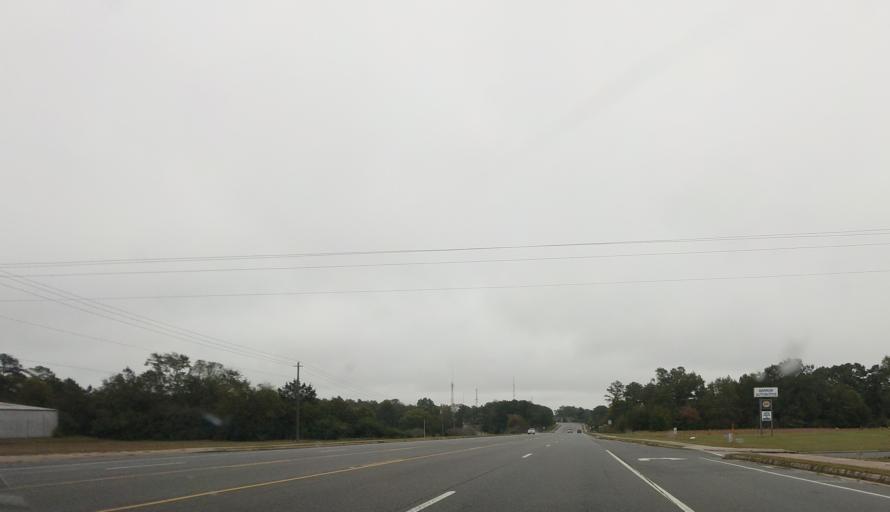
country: US
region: Georgia
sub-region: Taylor County
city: Reynolds
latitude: 32.5601
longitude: -84.1058
